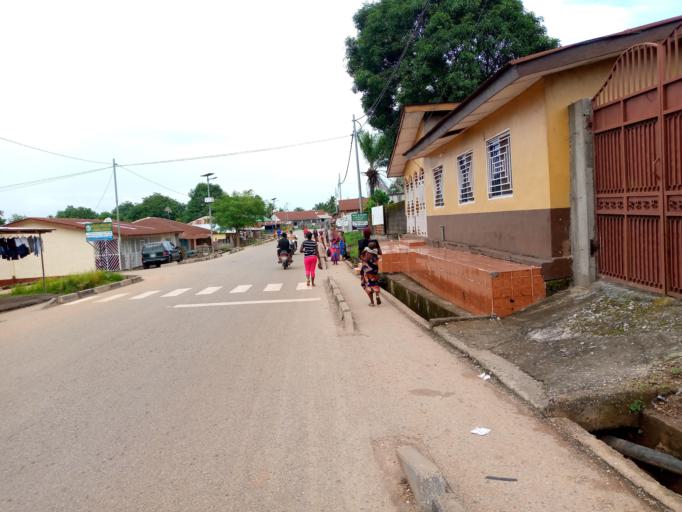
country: SL
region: Northern Province
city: Magburaka
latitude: 8.7215
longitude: -11.9520
